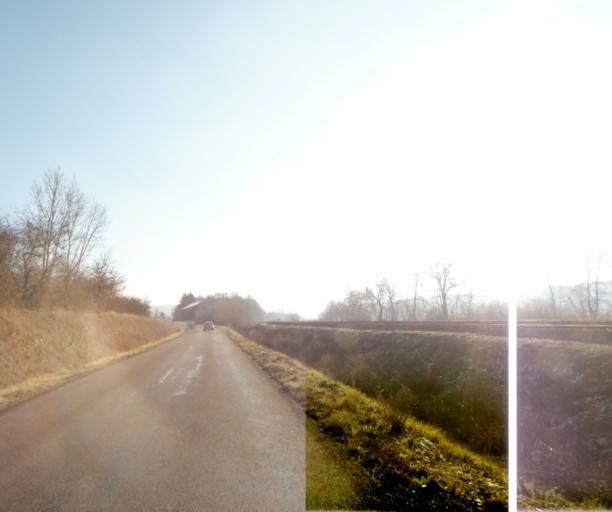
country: FR
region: Champagne-Ardenne
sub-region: Departement de la Haute-Marne
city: Chevillon
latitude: 48.5033
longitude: 5.1269
